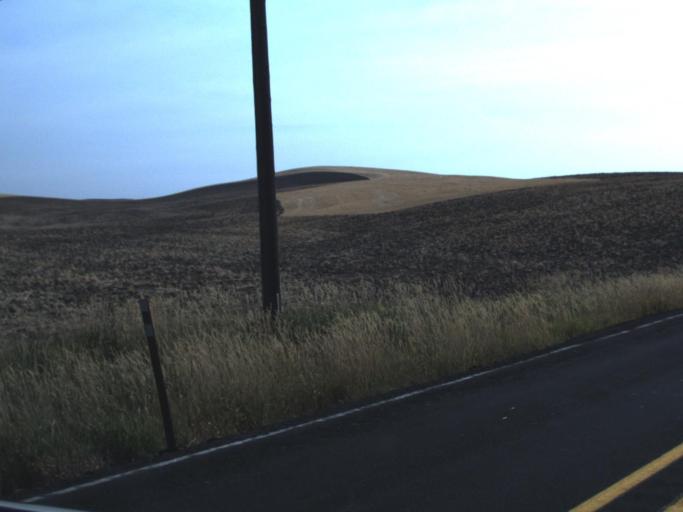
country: US
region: Washington
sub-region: Whitman County
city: Colfax
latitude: 47.0275
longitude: -117.1494
